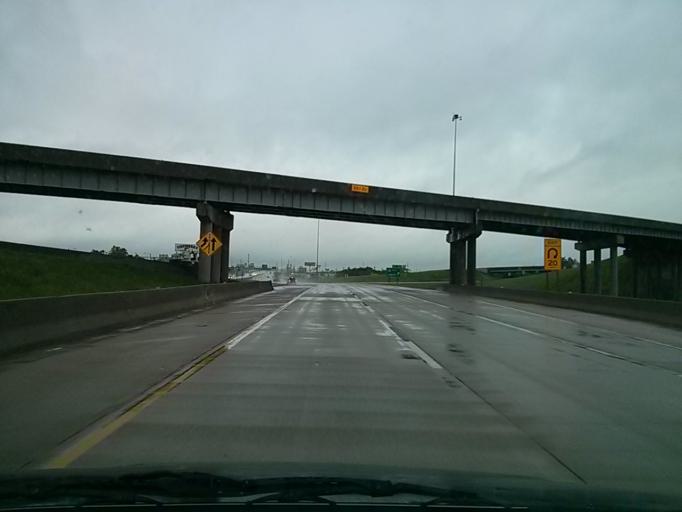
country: US
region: Oklahoma
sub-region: Tulsa County
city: Oakhurst
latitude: 36.0891
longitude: -96.0398
